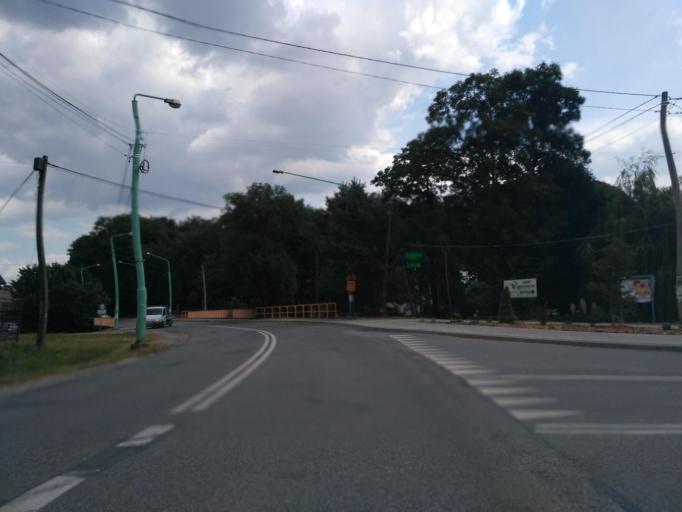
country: PL
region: Subcarpathian Voivodeship
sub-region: Powiat debicki
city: Zyrakow
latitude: 50.0617
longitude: 21.3573
